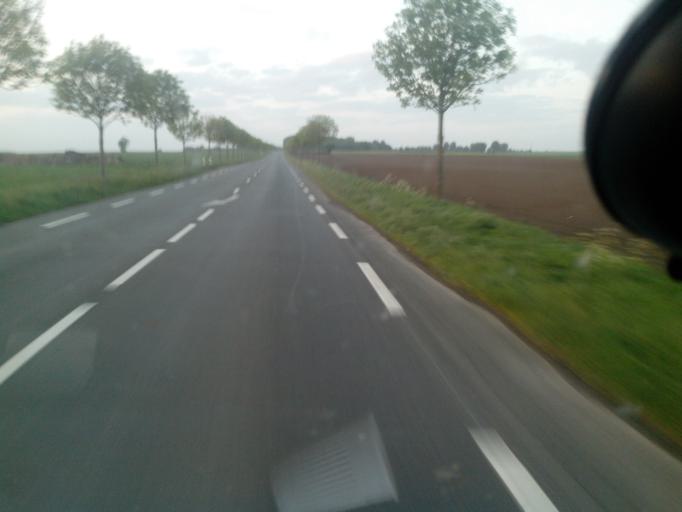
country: FR
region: Nord-Pas-de-Calais
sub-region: Departement du Pas-de-Calais
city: Marconnelle
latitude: 50.2955
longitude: 1.9987
